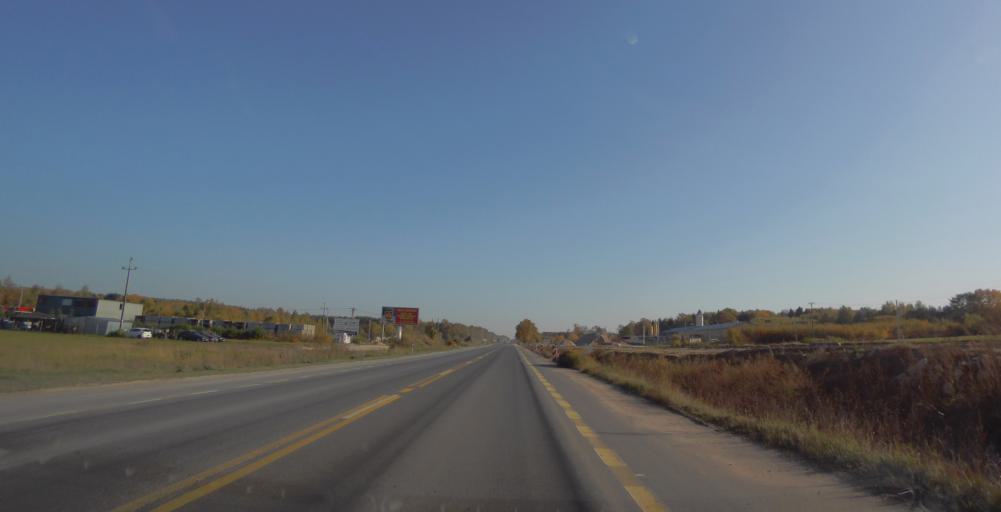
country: PL
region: Masovian Voivodeship
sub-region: Powiat otwocki
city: Celestynow
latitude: 52.0945
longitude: 21.4141
